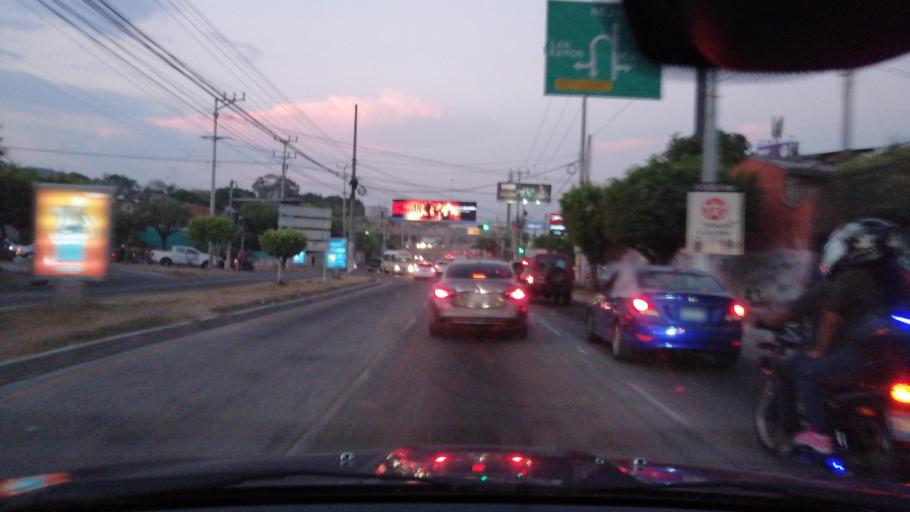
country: SV
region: San Salvador
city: Mejicanos
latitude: 13.7338
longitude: -89.2179
